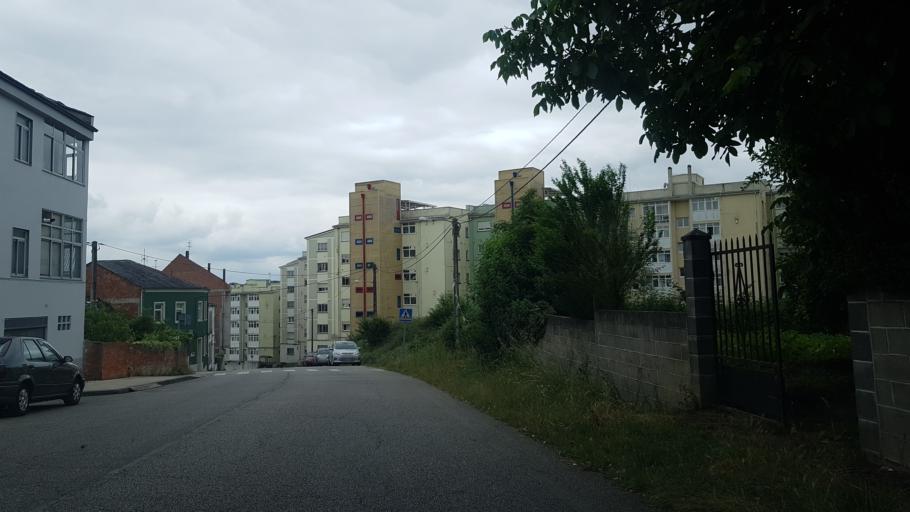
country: ES
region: Galicia
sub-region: Provincia de Lugo
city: Lugo
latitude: 43.0187
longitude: -7.5496
